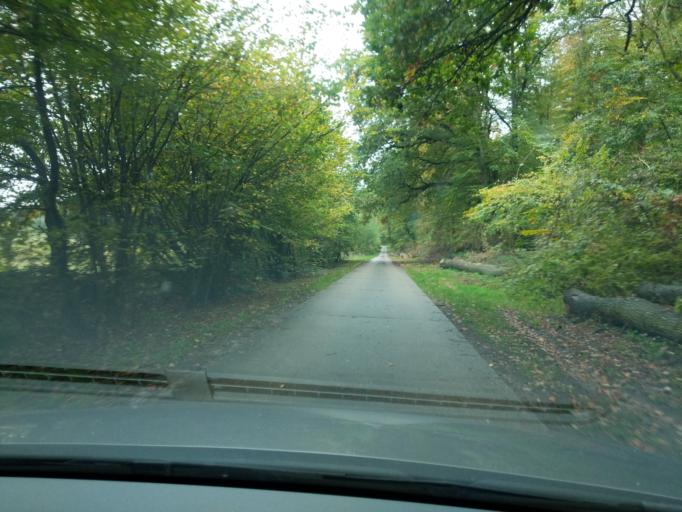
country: DE
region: Schleswig-Holstein
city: Buchhorst
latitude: 53.3965
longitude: 10.5591
